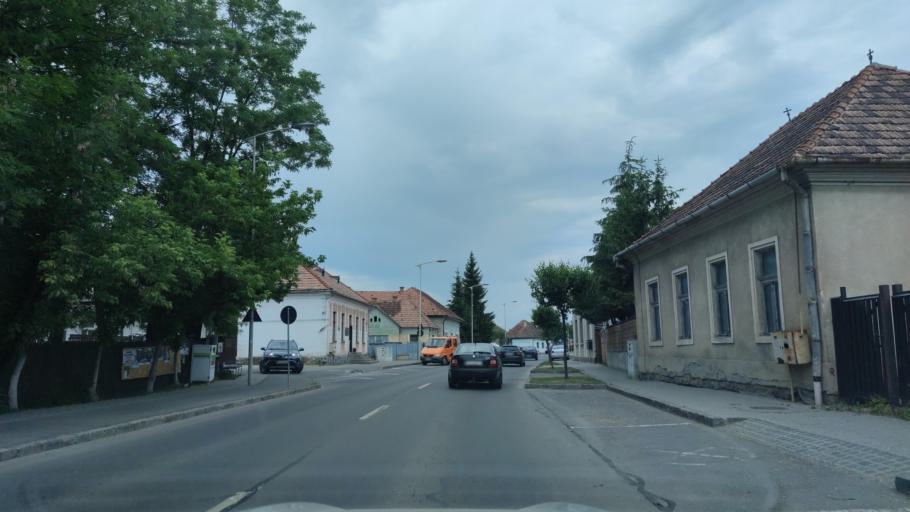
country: RO
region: Harghita
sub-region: Municipiul Miercurea Ciuc
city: Miercurea-Ciuc
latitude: 46.3760
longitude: 25.8012
